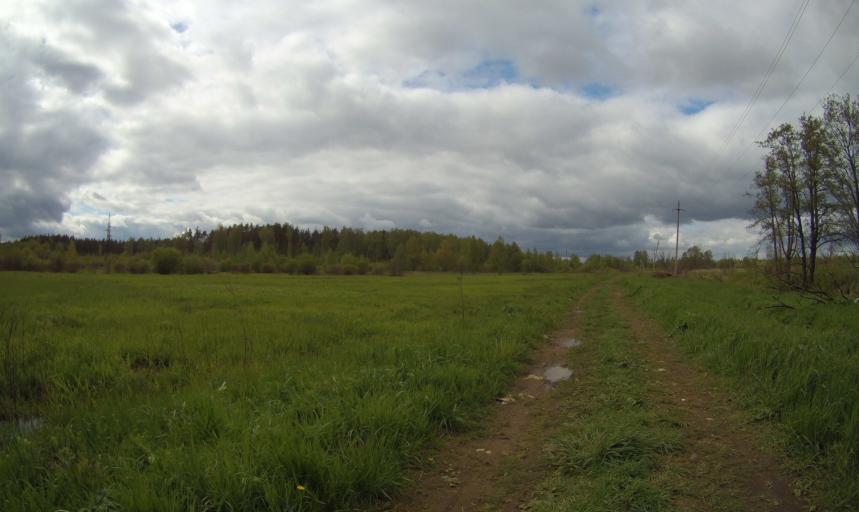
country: RU
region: Moskovskaya
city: Rechitsy
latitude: 55.5672
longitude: 38.4804
